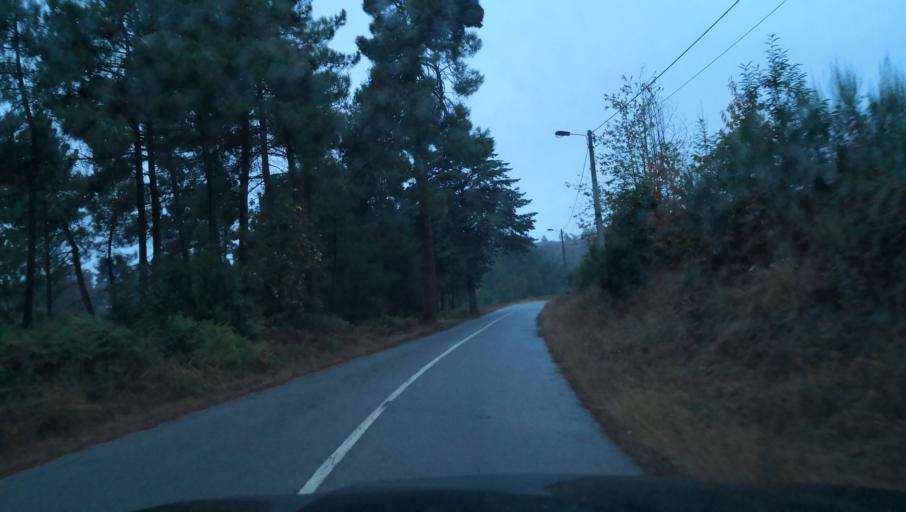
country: PT
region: Vila Real
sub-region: Sabrosa
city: Sabrosa
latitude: 41.2642
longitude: -7.6045
